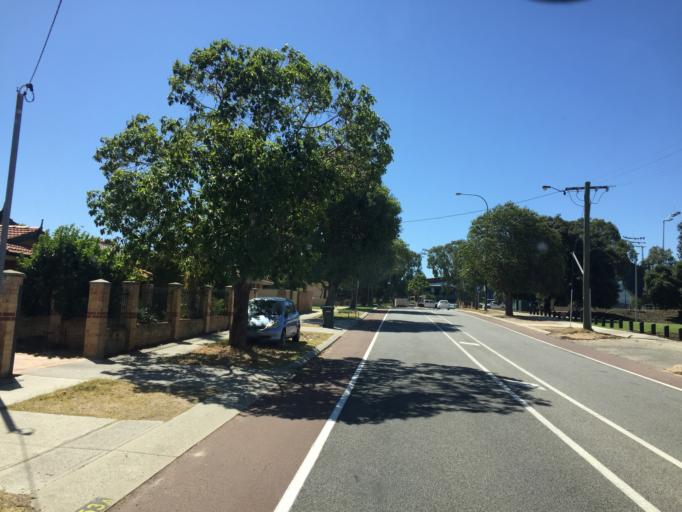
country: AU
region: Western Australia
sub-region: Victoria Park
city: Victoria Park
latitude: -31.9752
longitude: 115.9094
